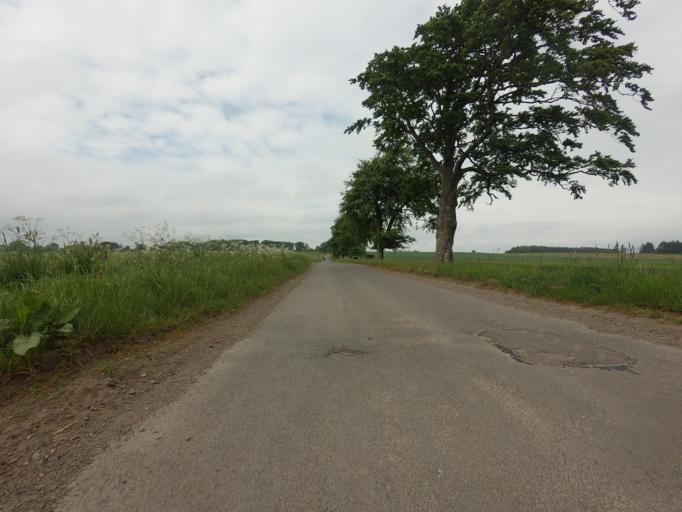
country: GB
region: Scotland
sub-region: Perth and Kinross
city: Kinross
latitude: 56.1778
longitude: -3.4386
